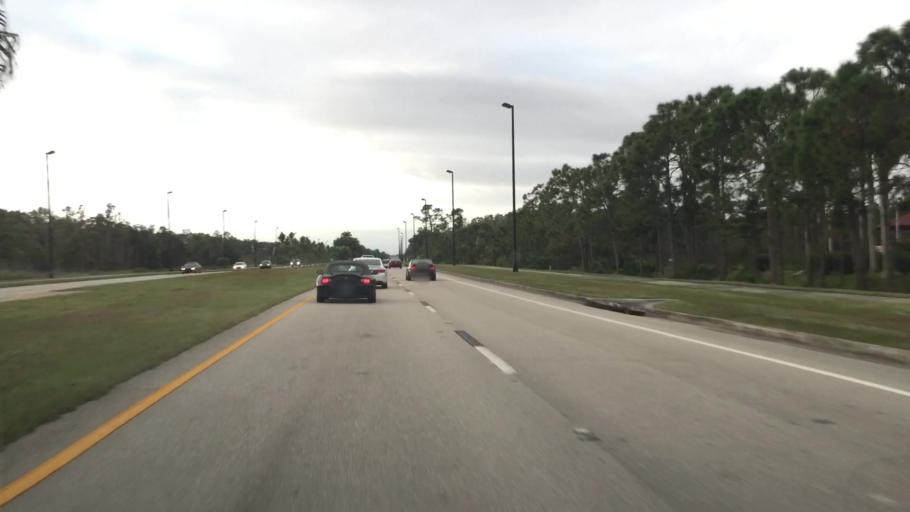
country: US
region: Florida
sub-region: Lee County
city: Three Oaks
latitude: 26.5282
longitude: -81.7857
